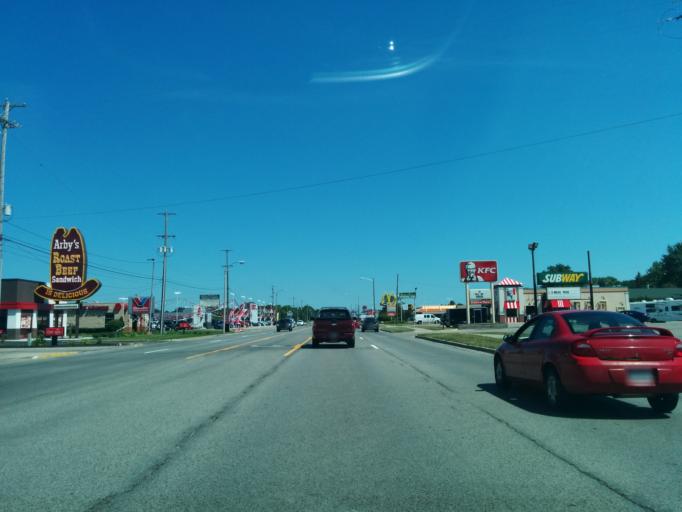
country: US
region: Michigan
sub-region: Bay County
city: Bay City
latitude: 43.6115
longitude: -83.9147
